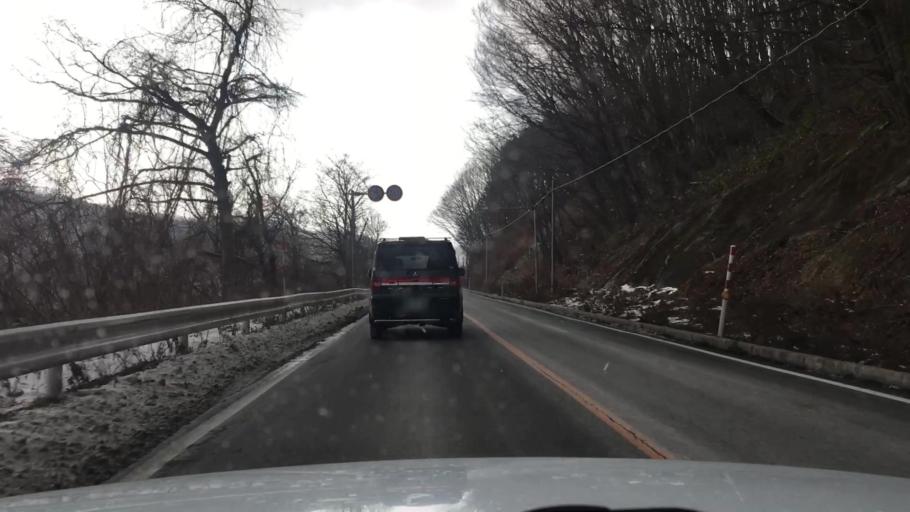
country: JP
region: Iwate
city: Morioka-shi
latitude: 39.6629
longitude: 141.3306
